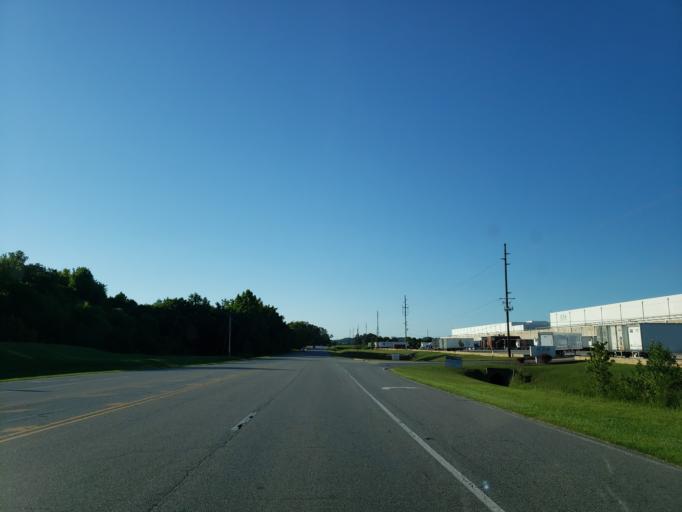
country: US
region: Georgia
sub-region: Polk County
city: Rockmart
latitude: 34.0227
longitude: -85.0499
